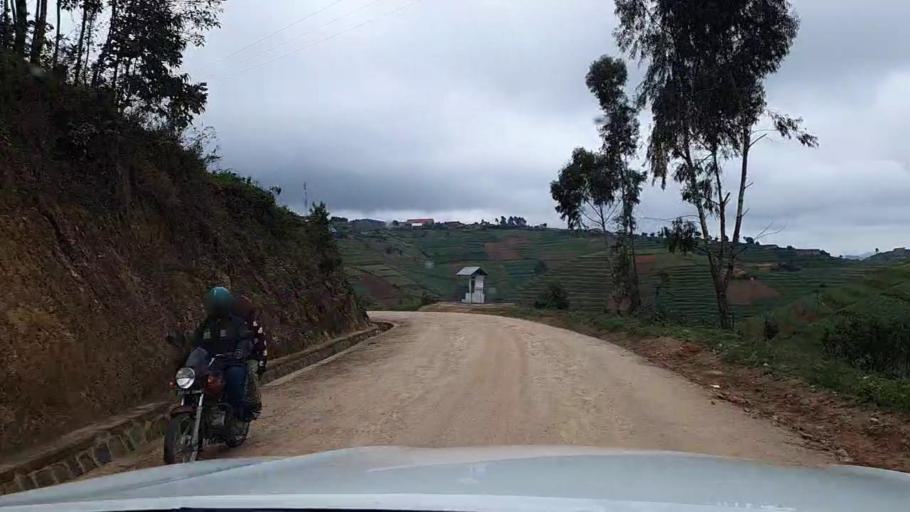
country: RW
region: Southern Province
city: Nzega
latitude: -2.3786
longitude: 29.3828
